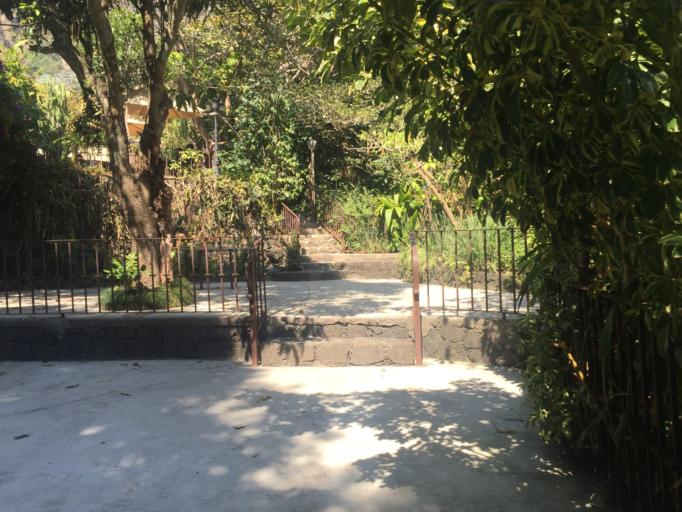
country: MX
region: Morelos
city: Tepoztlan
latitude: 18.9943
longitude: -99.0993
